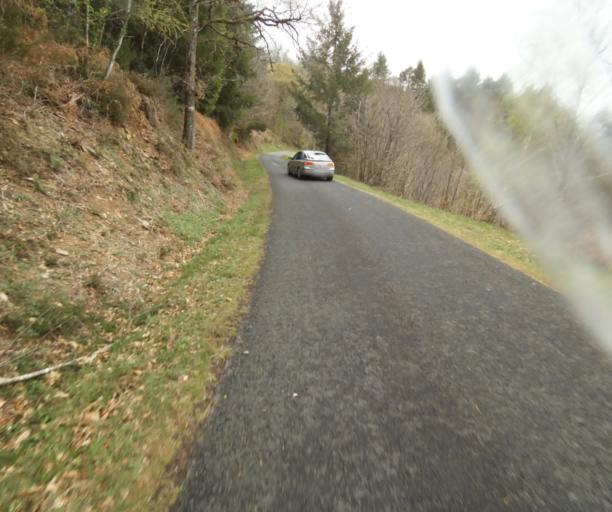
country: FR
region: Limousin
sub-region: Departement de la Correze
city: Naves
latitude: 45.3002
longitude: 1.8101
